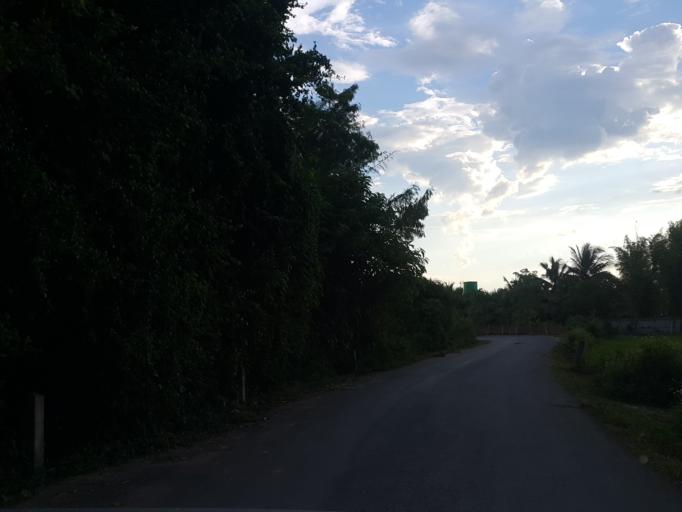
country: TH
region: Chiang Mai
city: San Sai
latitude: 18.8882
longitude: 99.0721
